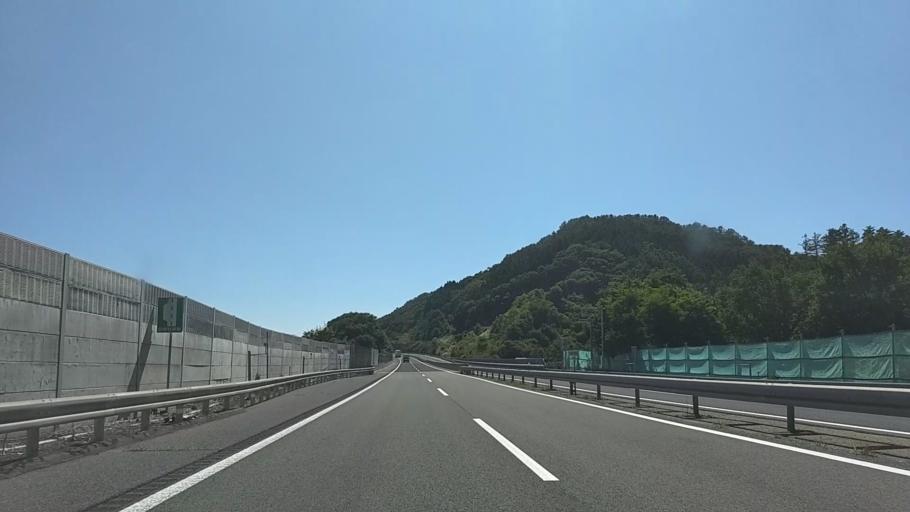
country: JP
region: Nagano
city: Nakano
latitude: 36.7695
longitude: 138.3176
